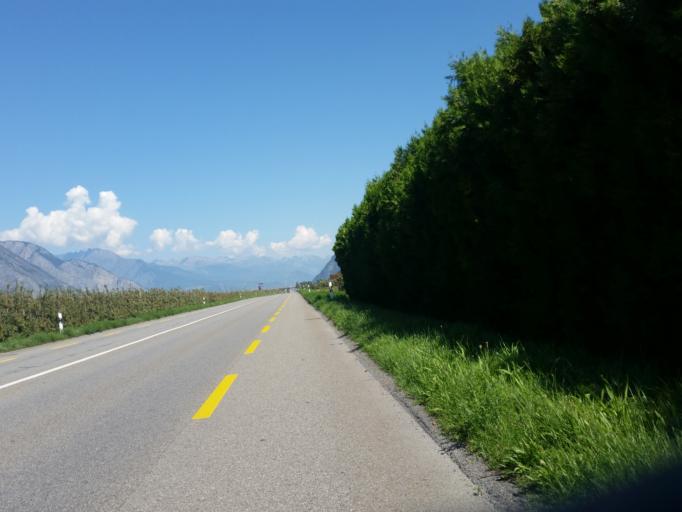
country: CH
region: Valais
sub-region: Martigny District
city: Charrat-les-Chenes
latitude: 46.1310
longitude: 7.1368
